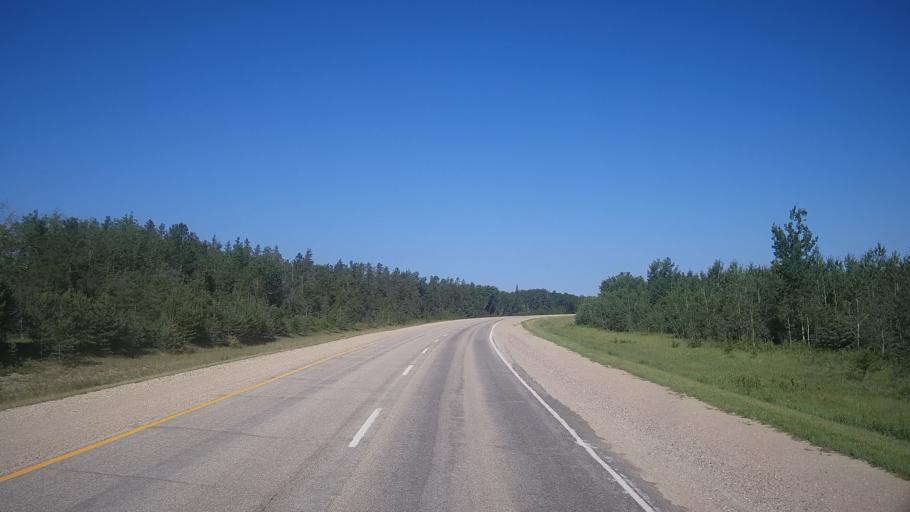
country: CA
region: Manitoba
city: La Broquerie
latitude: 49.6494
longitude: -95.9715
